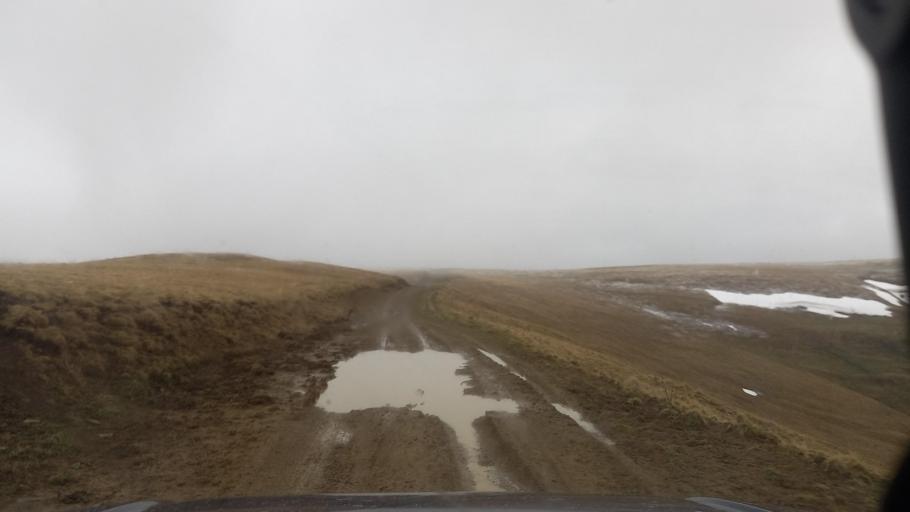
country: RU
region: Kabardino-Balkariya
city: Terskol
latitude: 43.5894
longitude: 42.4741
